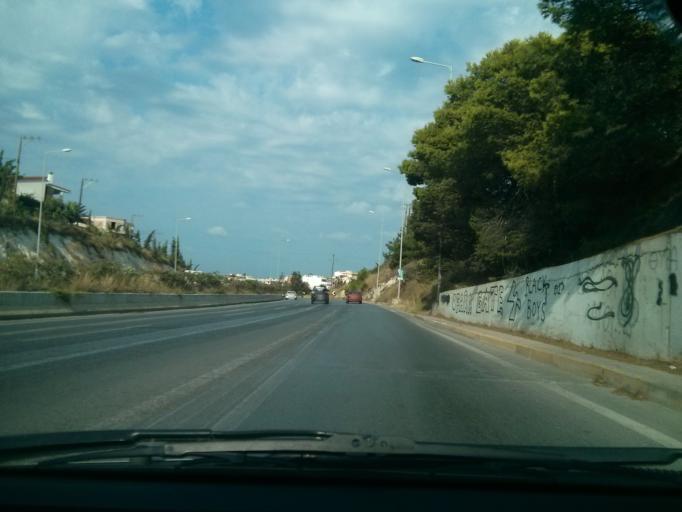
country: GR
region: Crete
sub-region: Nomos Irakleiou
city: Irakleion
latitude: 35.3213
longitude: 25.1468
